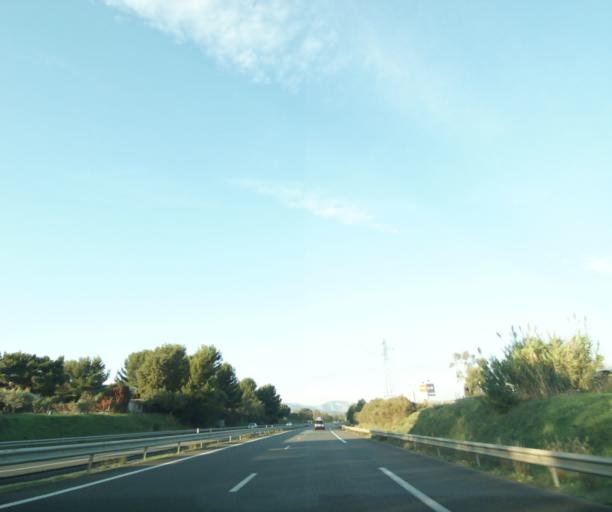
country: FR
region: Provence-Alpes-Cote d'Azur
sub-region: Departement des Bouches-du-Rhone
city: Aubagne
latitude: 43.2889
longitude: 5.5867
